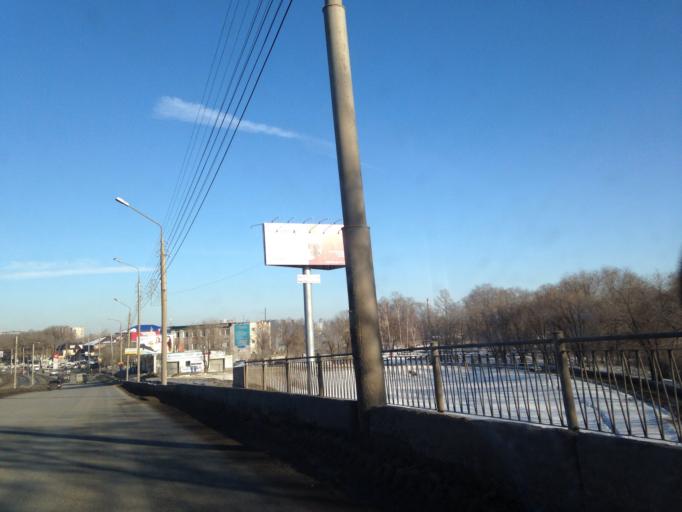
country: RU
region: Ulyanovsk
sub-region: Ulyanovskiy Rayon
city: Ulyanovsk
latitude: 54.2941
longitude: 48.3169
